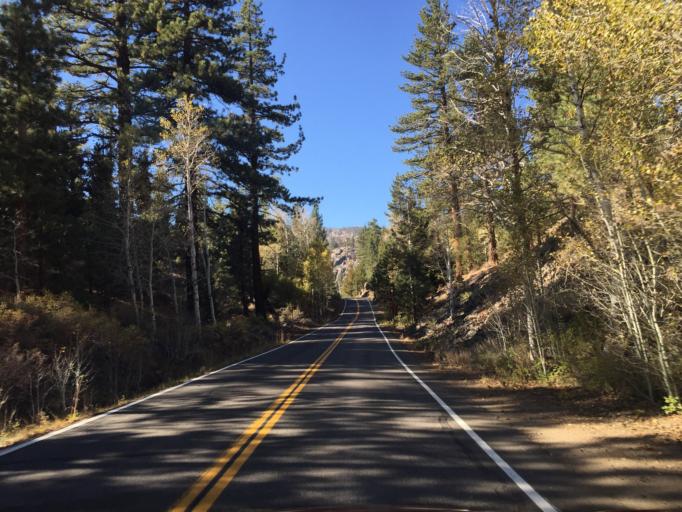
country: US
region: California
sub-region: Mono County
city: Bridgeport
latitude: 38.3383
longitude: -119.5501
